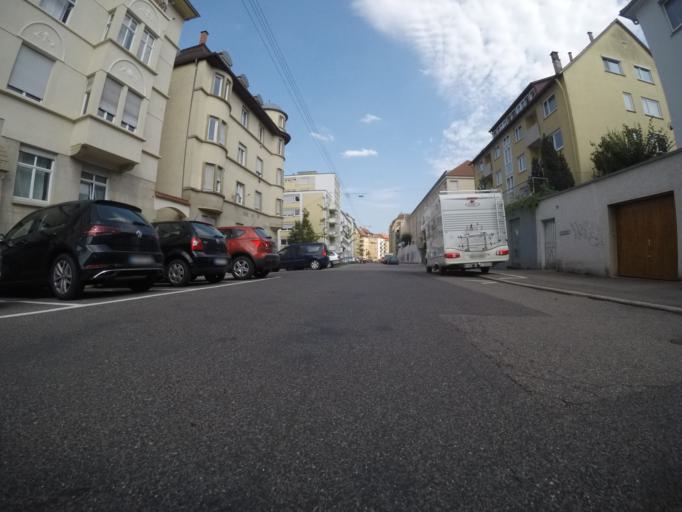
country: DE
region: Baden-Wuerttemberg
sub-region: Regierungsbezirk Stuttgart
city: Stuttgart
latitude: 48.7740
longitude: 9.1500
